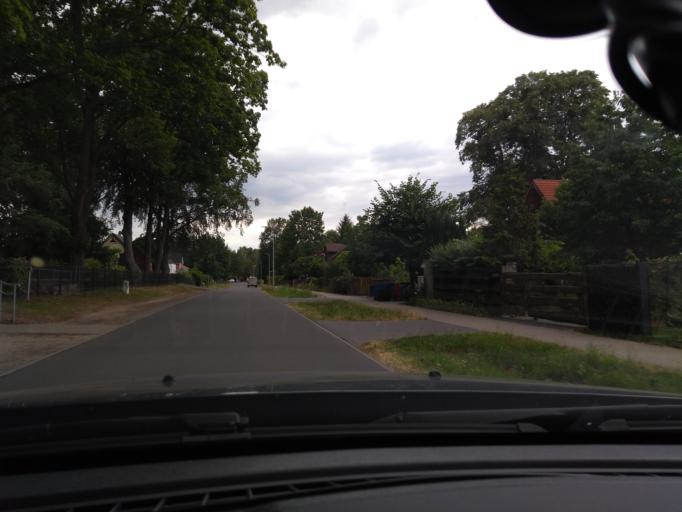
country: DE
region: Brandenburg
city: Dallgow-Doeberitz
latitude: 52.5580
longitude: 13.0660
